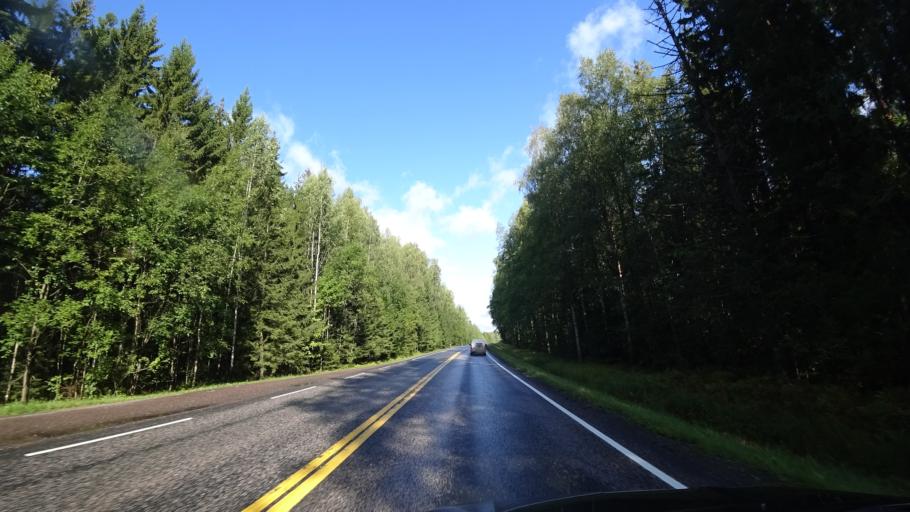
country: FI
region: Uusimaa
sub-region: Helsinki
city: Tuusula
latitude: 60.4506
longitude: 24.9589
